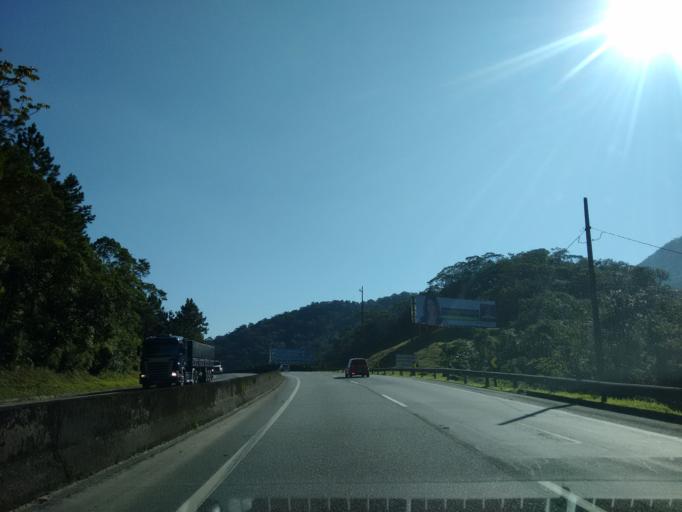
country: BR
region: Parana
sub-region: Guaratuba
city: Guaratuba
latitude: -25.9561
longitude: -48.9010
